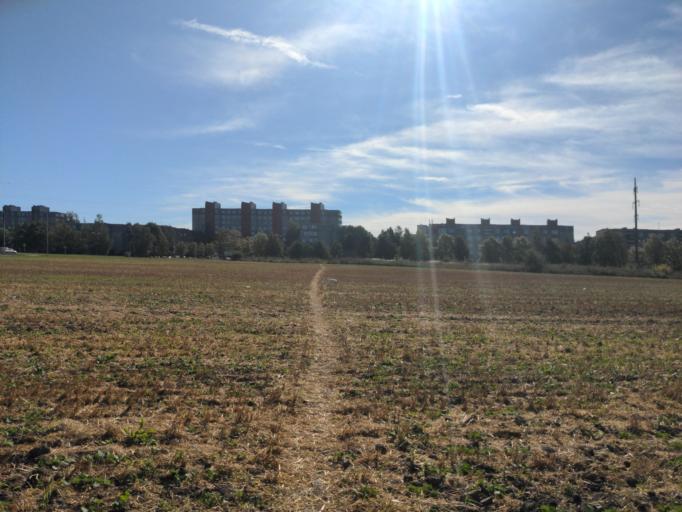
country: LT
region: Siauliu apskritis
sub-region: Siauliai
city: Siauliai
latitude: 55.9195
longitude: 23.2533
